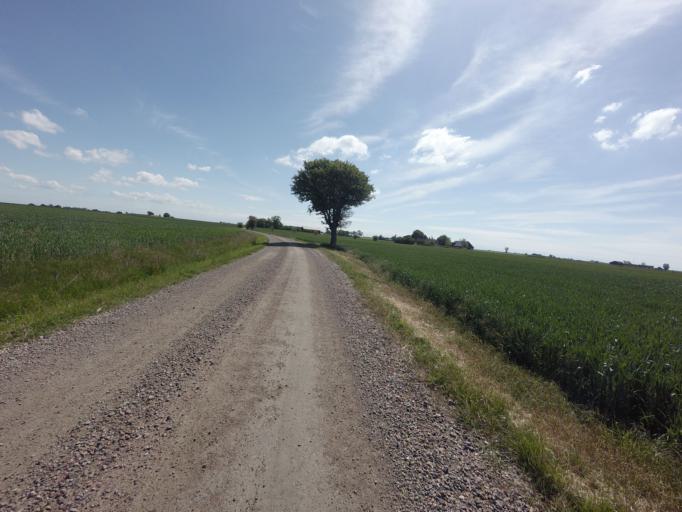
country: SE
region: Skane
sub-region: Trelleborgs Kommun
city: Skare
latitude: 55.4138
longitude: 13.0428
